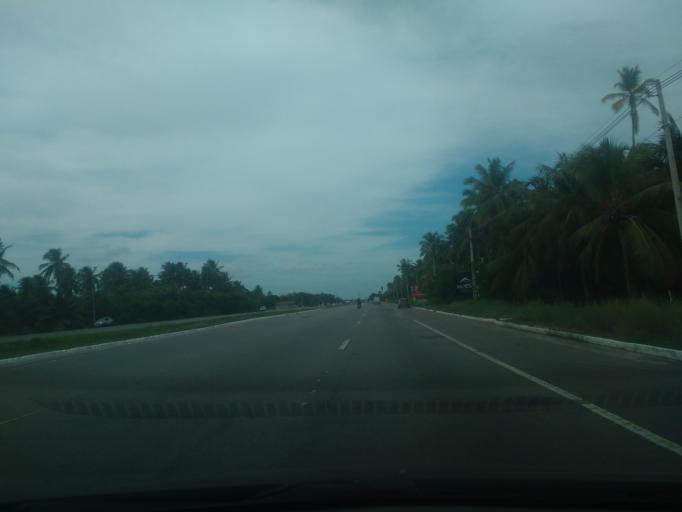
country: BR
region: Alagoas
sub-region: Marechal Deodoro
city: Marechal Deodoro
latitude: -9.7067
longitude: -35.8111
